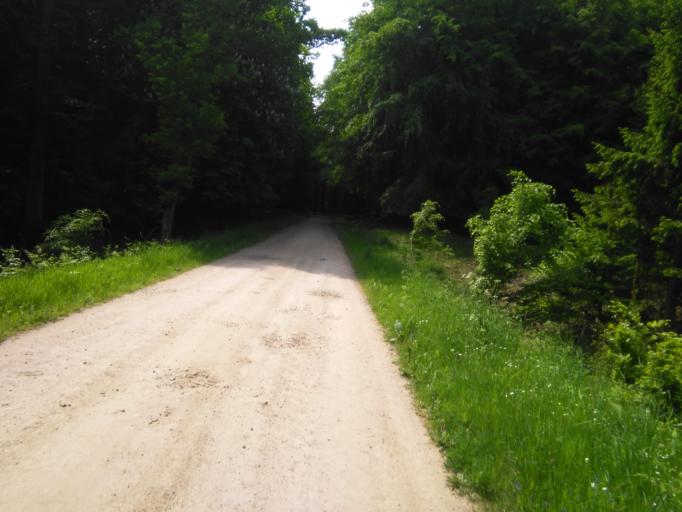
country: DK
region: Central Jutland
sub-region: Favrskov Kommune
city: Hammel
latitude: 56.2676
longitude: 9.9386
